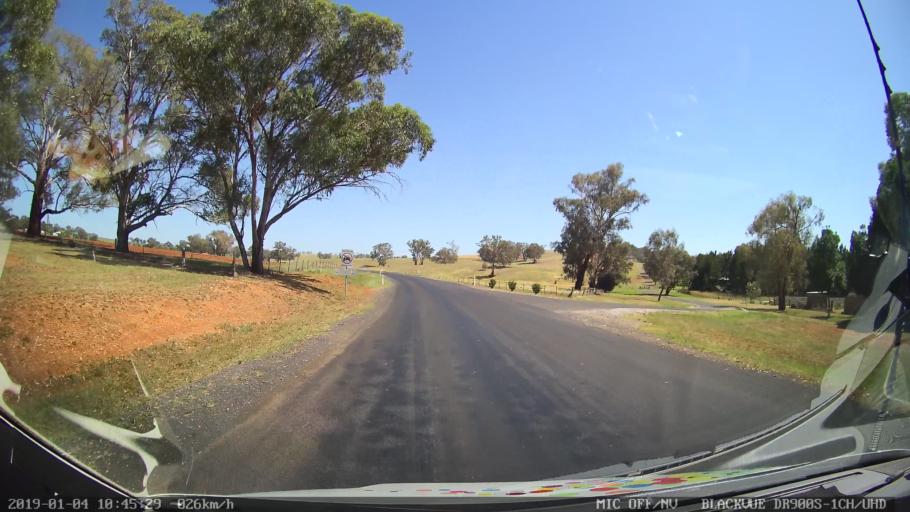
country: AU
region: New South Wales
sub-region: Cabonne
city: Molong
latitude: -33.2882
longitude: 148.7293
